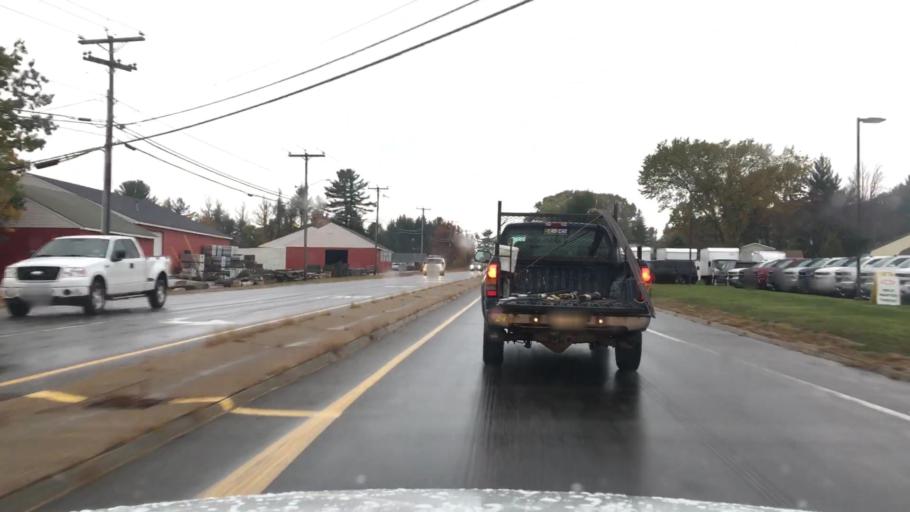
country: US
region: New Hampshire
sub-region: Strafford County
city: Somersworth
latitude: 43.2654
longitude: -70.9068
